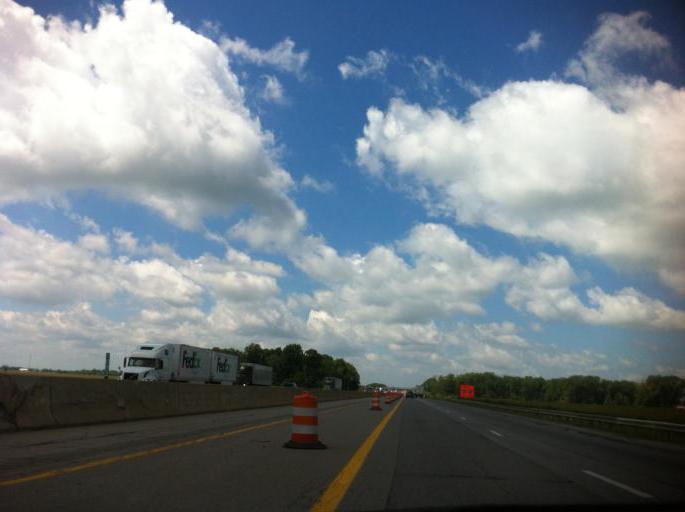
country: US
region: Ohio
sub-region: Huron County
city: Bellevue
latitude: 41.3473
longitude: -82.8036
